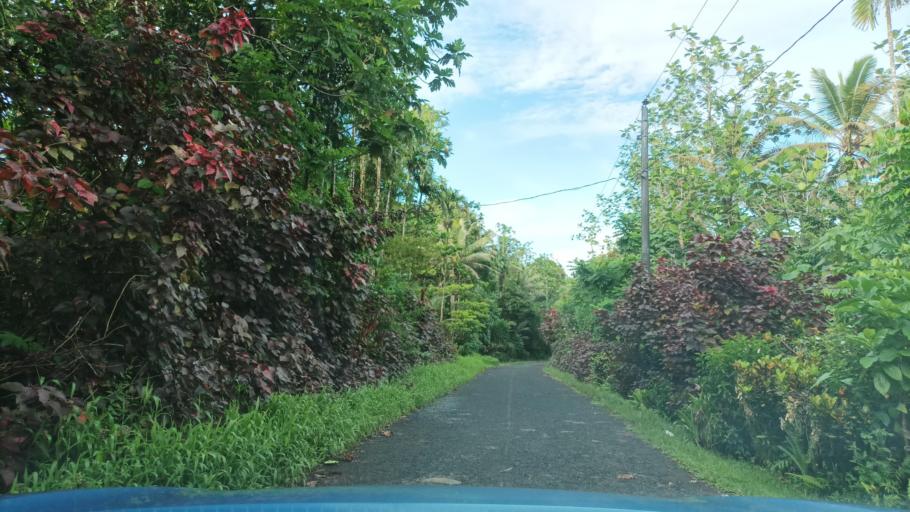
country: FM
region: Pohnpei
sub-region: Sokehs Municipality
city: Palikir - National Government Center
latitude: 6.9147
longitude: 158.1417
